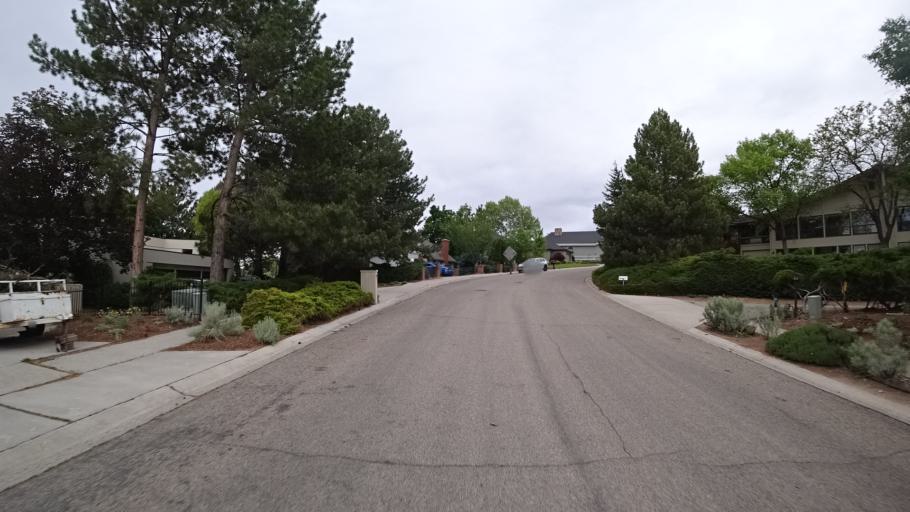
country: US
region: Idaho
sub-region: Ada County
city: Boise
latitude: 43.6150
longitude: -116.1719
